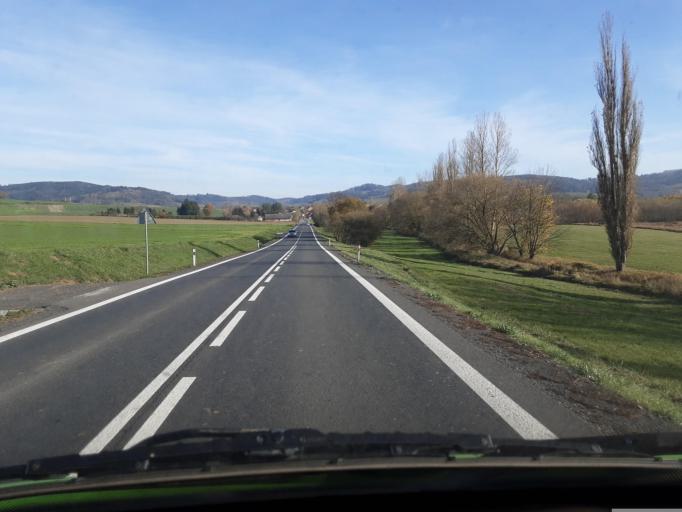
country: CZ
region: Plzensky
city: Klatovy
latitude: 49.3638
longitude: 13.3421
